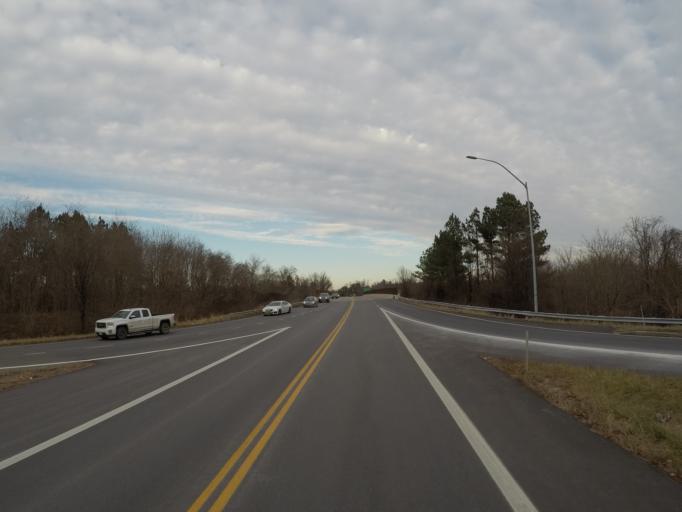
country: US
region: Maryland
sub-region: Howard County
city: Riverside
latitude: 39.1720
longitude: -76.8515
